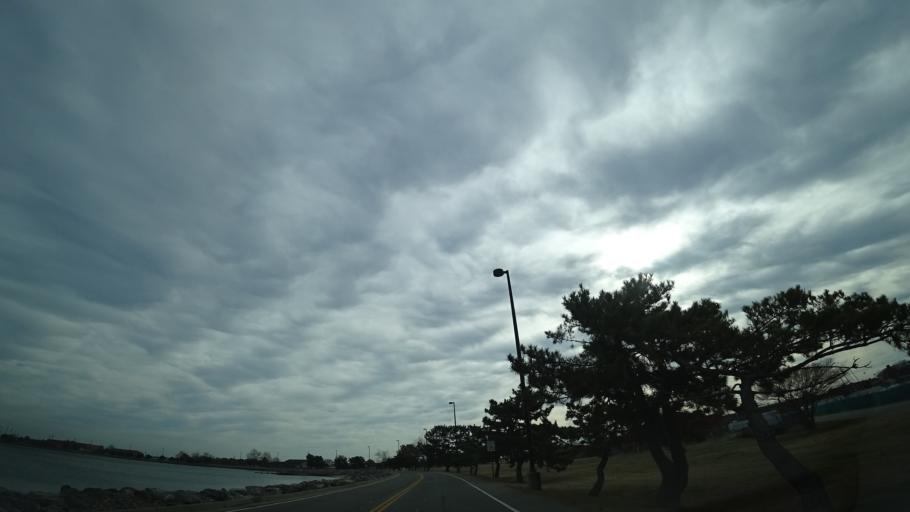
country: US
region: Virginia
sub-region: City of Hampton
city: East Hampton
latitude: 37.0095
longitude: -76.3096
